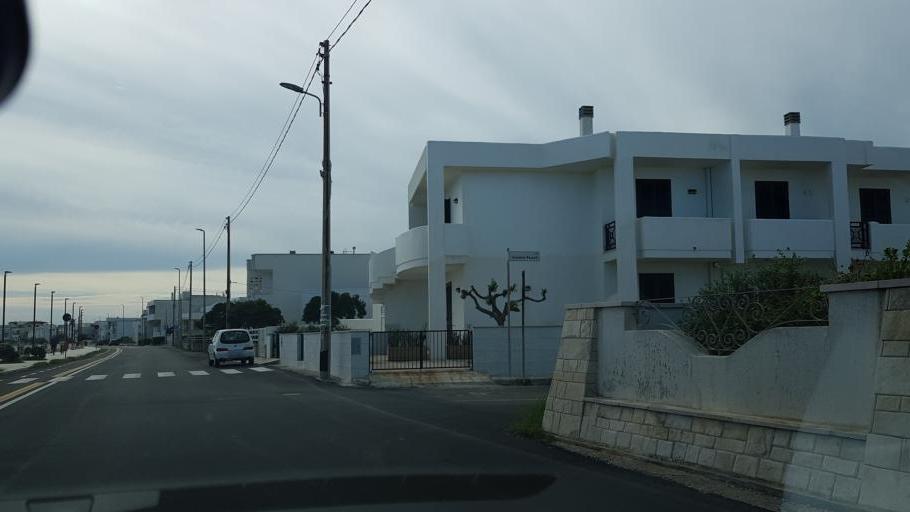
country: IT
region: Apulia
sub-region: Provincia di Lecce
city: Borgagne
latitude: 40.3058
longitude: 18.3982
